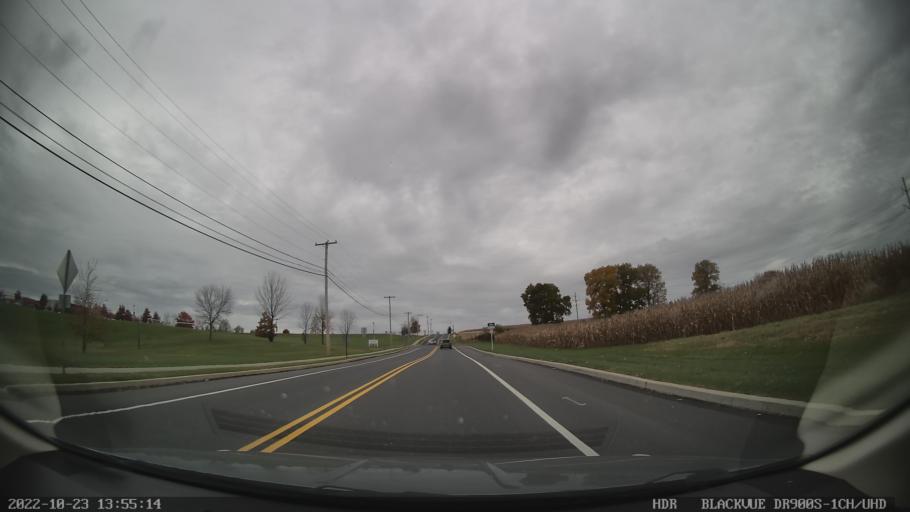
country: US
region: Pennsylvania
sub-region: Northampton County
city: North Catasauqua
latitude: 40.6780
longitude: -75.4627
